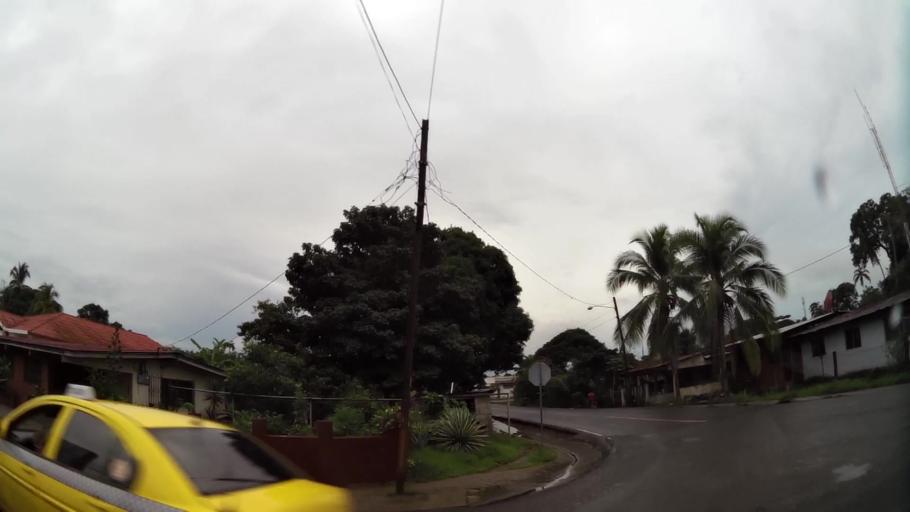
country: PA
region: Veraguas
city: Santiago de Veraguas
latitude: 8.1064
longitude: -80.9754
